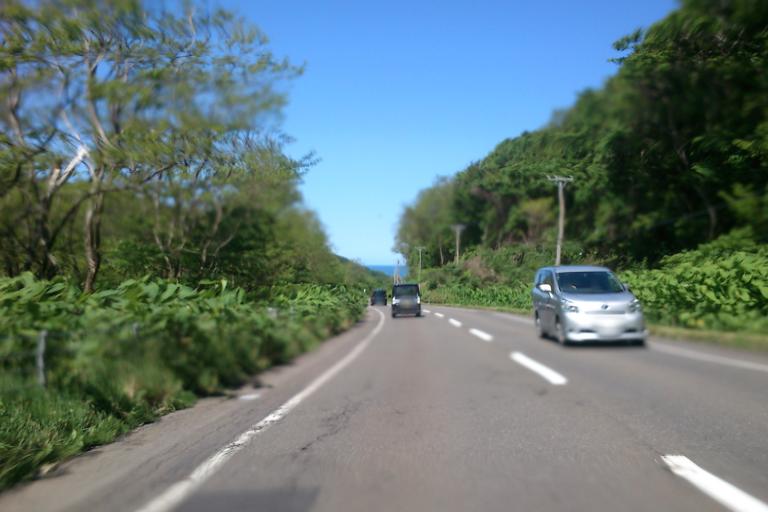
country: JP
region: Hokkaido
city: Ishikari
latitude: 43.5554
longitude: 141.4003
